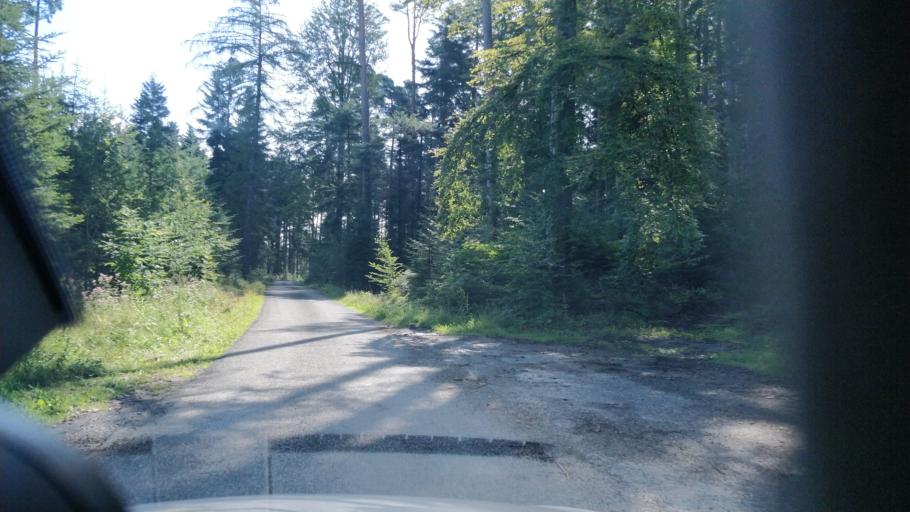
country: DE
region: Baden-Wuerttemberg
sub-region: Regierungsbezirk Stuttgart
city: Oberrot
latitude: 48.9936
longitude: 9.6620
